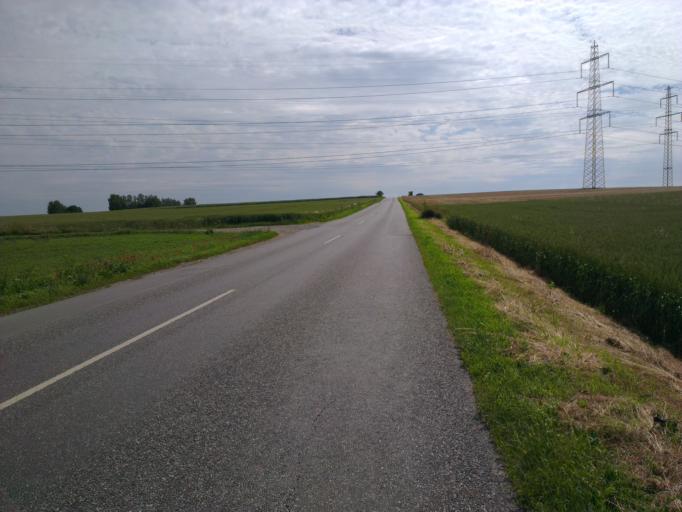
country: DK
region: Capital Region
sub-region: Frederikssund Kommune
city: Frederikssund
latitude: 55.7997
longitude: 12.0191
